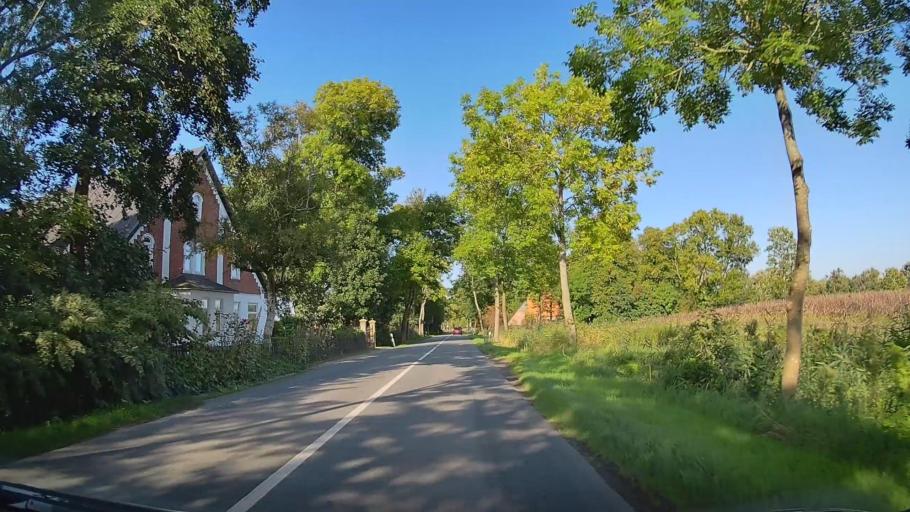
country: DE
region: Lower Saxony
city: Padingbuttel
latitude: 53.7247
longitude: 8.5395
